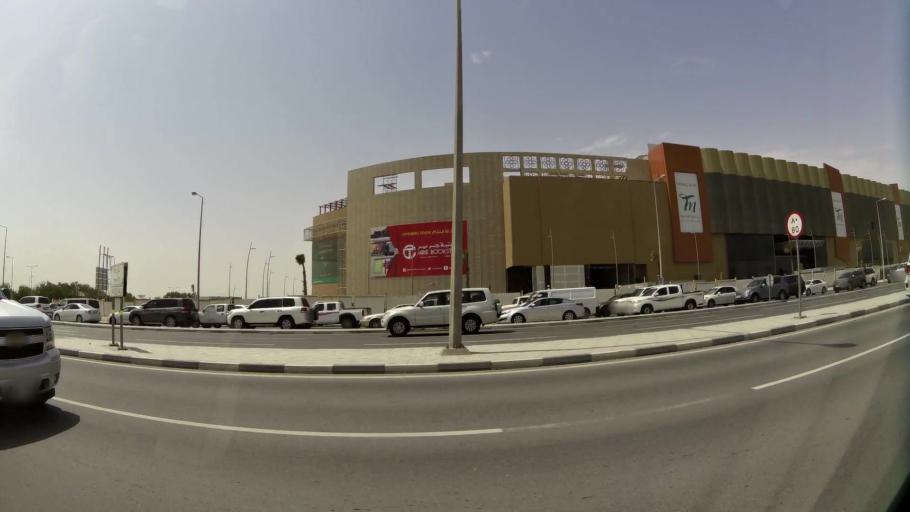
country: QA
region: Baladiyat ad Dawhah
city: Doha
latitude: 25.3363
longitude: 51.4821
